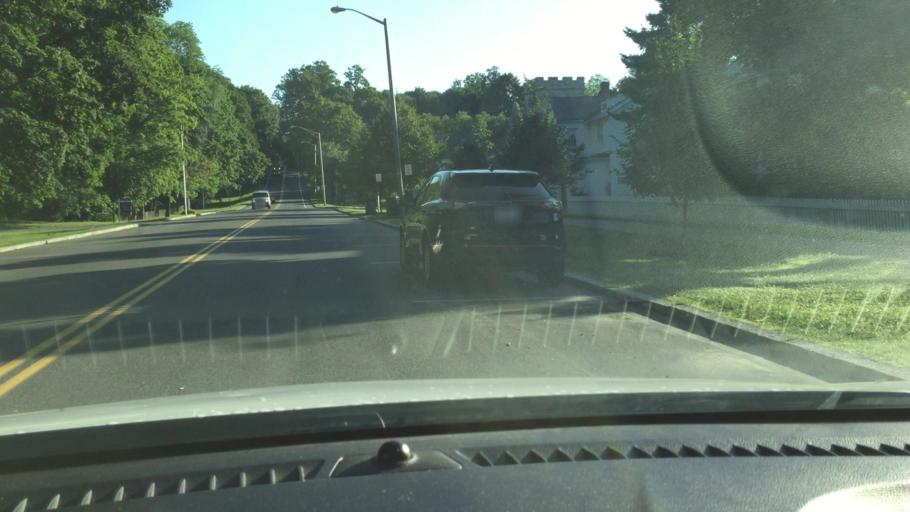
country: US
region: Massachusetts
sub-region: Berkshire County
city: Lenox
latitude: 42.3602
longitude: -73.2836
